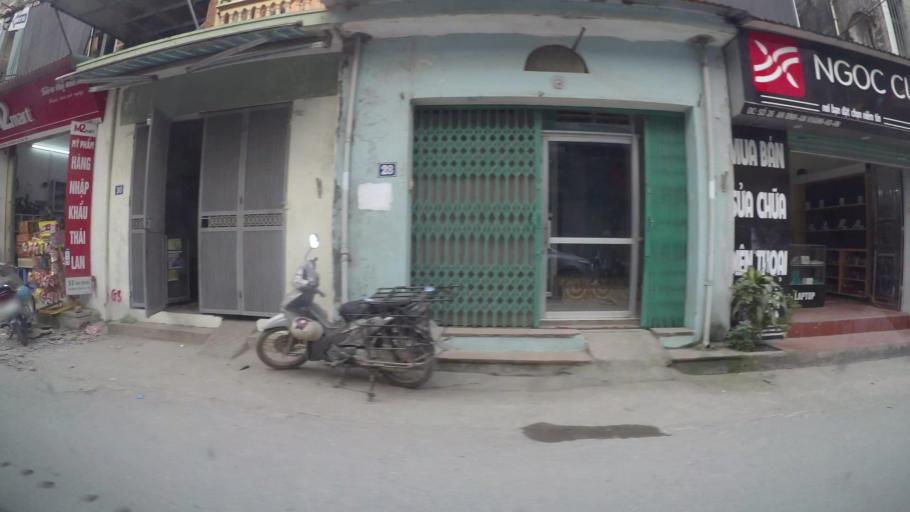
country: VN
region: Ha Noi
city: Ha Dong
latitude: 20.9926
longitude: 105.7298
